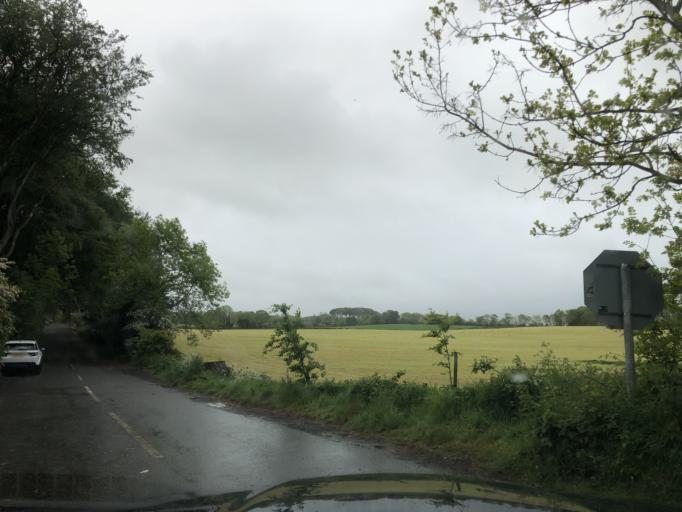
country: GB
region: Northern Ireland
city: Dunloy
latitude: 55.1368
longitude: -6.3847
